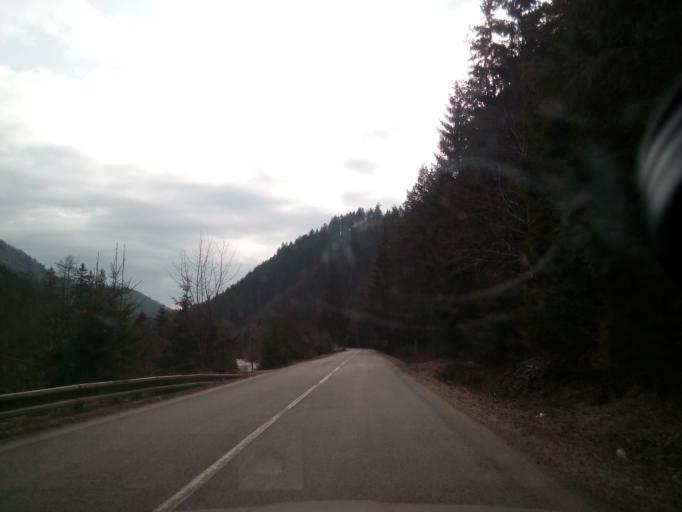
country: SK
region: Zilinsky
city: Oravska Lesna
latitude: 49.2567
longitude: 19.1528
